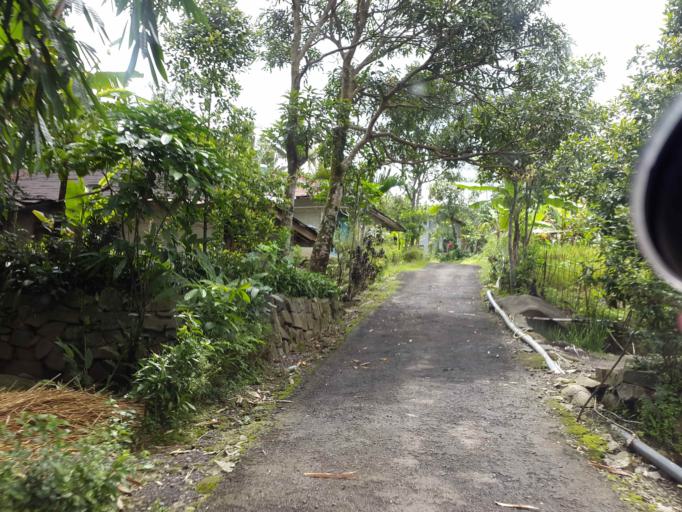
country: ID
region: Central Java
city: Randudongkal
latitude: -7.1554
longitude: 109.4149
